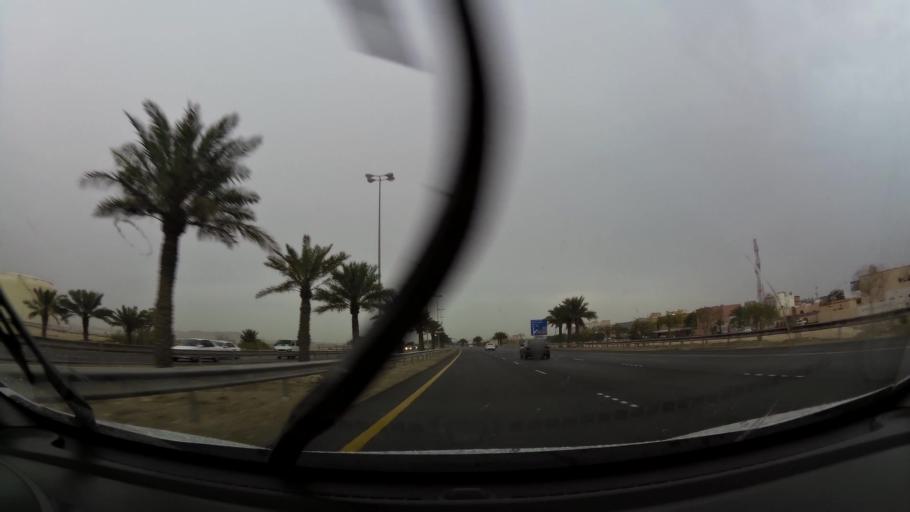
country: BH
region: Central Governorate
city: Dar Kulayb
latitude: 26.0730
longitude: 50.5148
